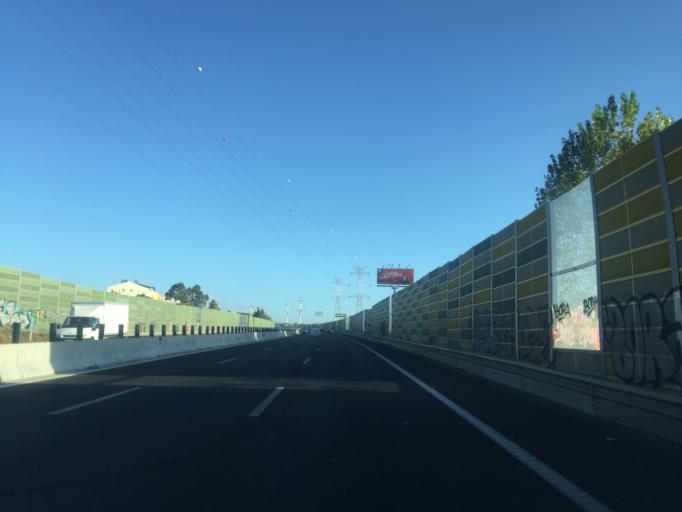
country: PT
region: Lisbon
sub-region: Loures
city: Bobadela
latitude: 38.8090
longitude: -9.1033
